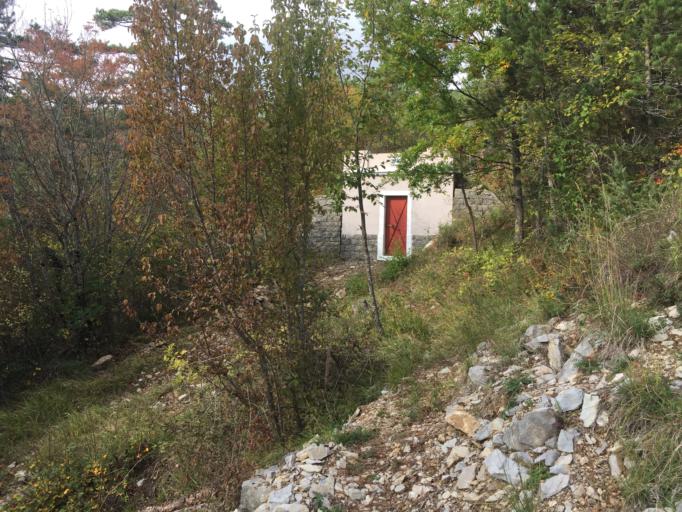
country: HR
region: Istarska
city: Buzet
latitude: 45.4102
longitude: 14.1161
